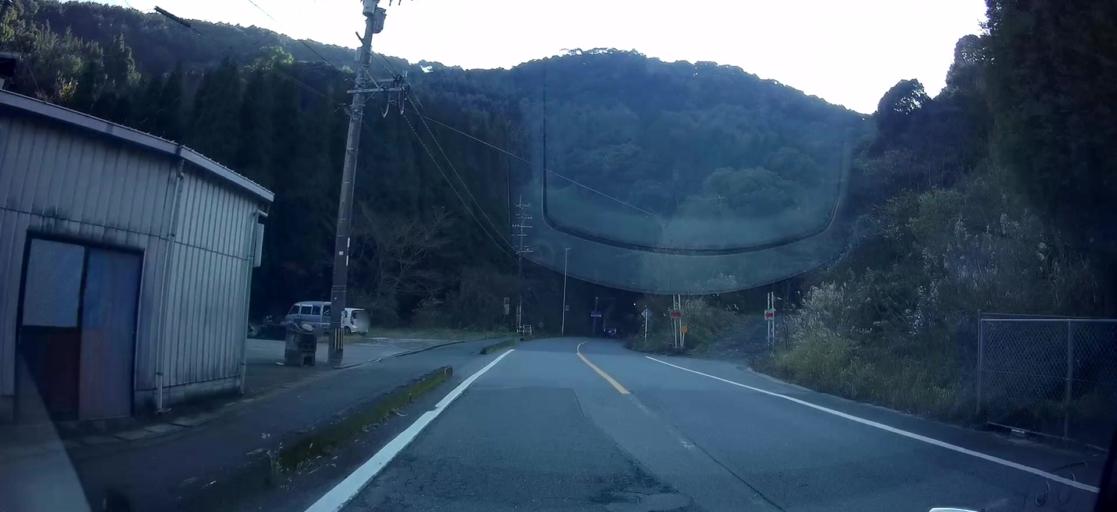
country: JP
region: Kumamoto
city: Hondo
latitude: 32.4333
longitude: 130.4055
